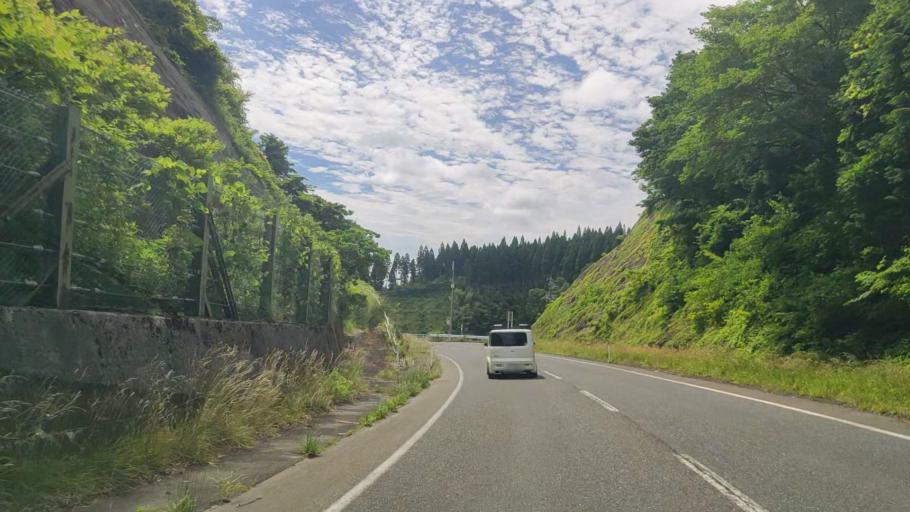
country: JP
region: Okayama
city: Niimi
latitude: 35.1733
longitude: 133.5721
